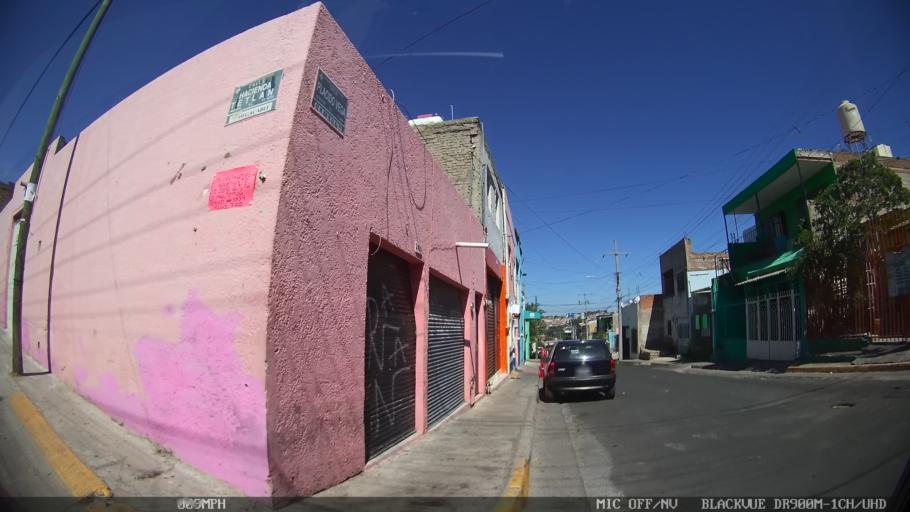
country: MX
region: Jalisco
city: Tlaquepaque
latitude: 20.6953
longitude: -103.2807
